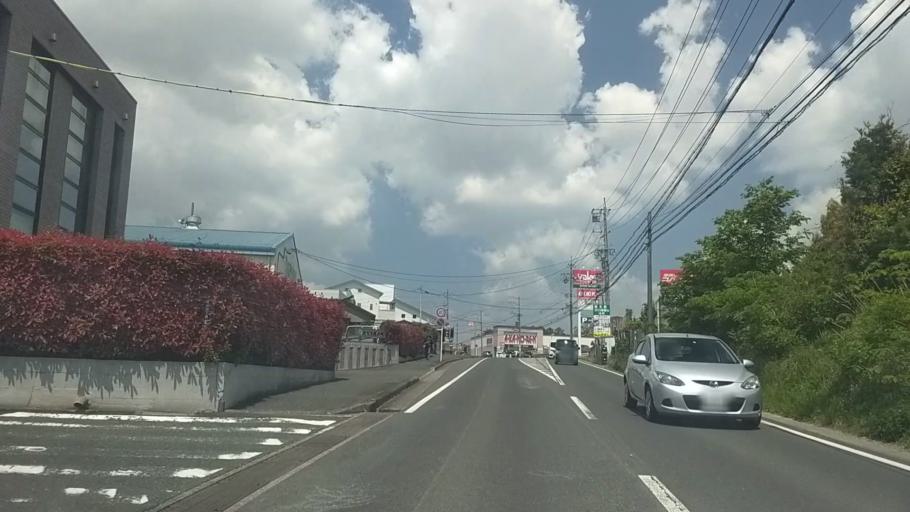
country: JP
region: Shizuoka
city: Hamamatsu
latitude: 34.7519
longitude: 137.7355
